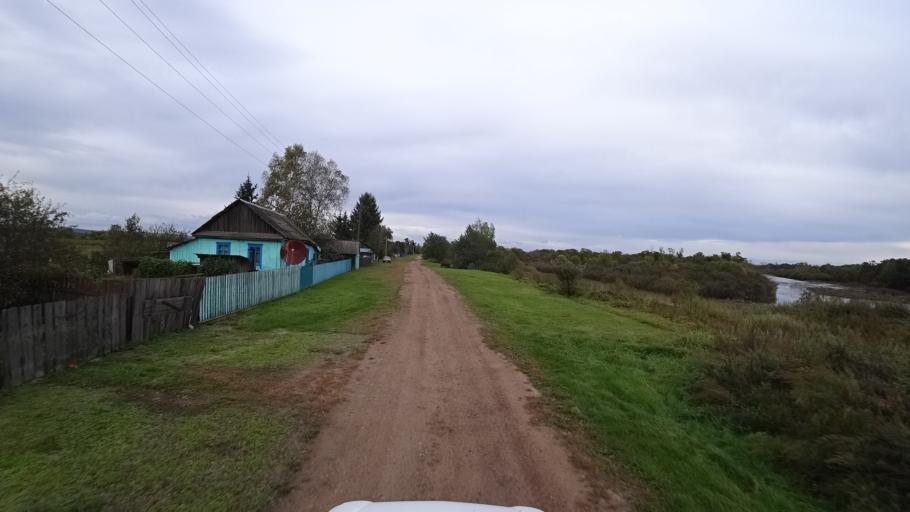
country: RU
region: Amur
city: Arkhara
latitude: 49.4328
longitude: 130.2607
